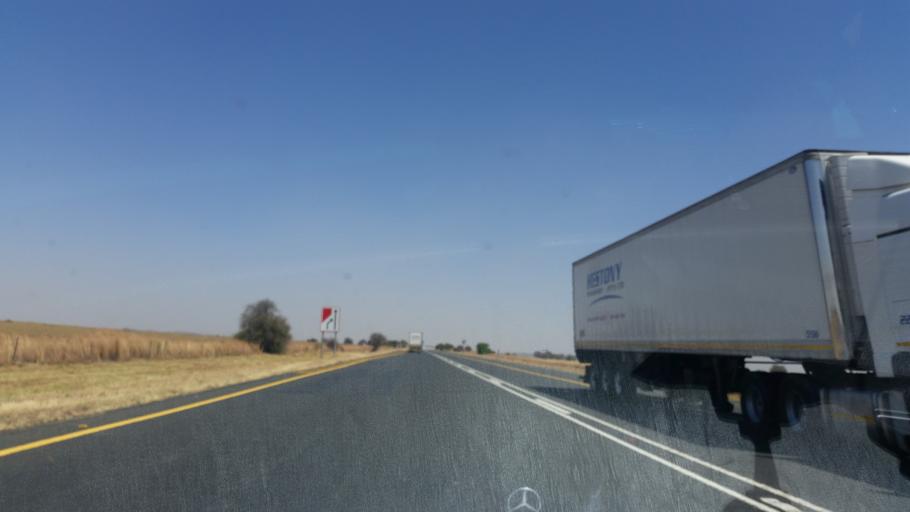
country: ZA
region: Orange Free State
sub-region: Lejweleputswa District Municipality
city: Winburg
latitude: -28.6474
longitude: 26.8802
